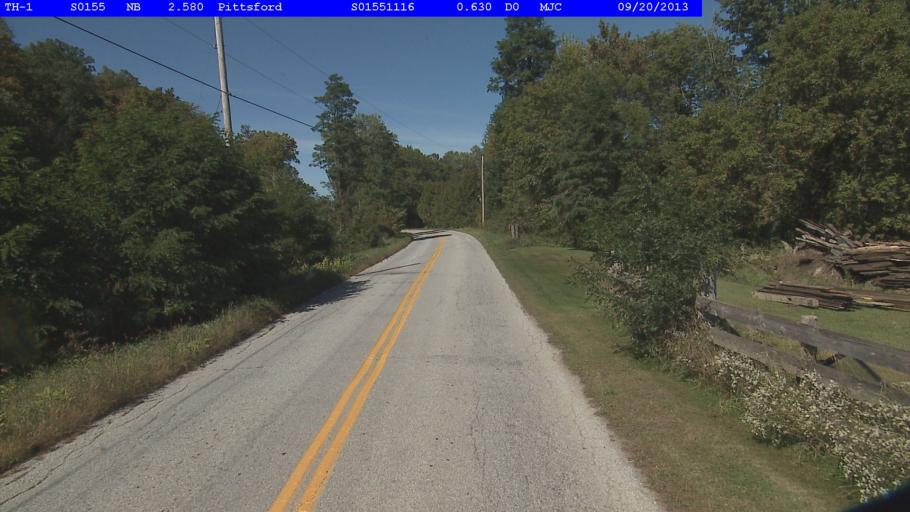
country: US
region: Vermont
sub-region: Rutland County
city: Brandon
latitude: 43.7011
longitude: -73.0442
